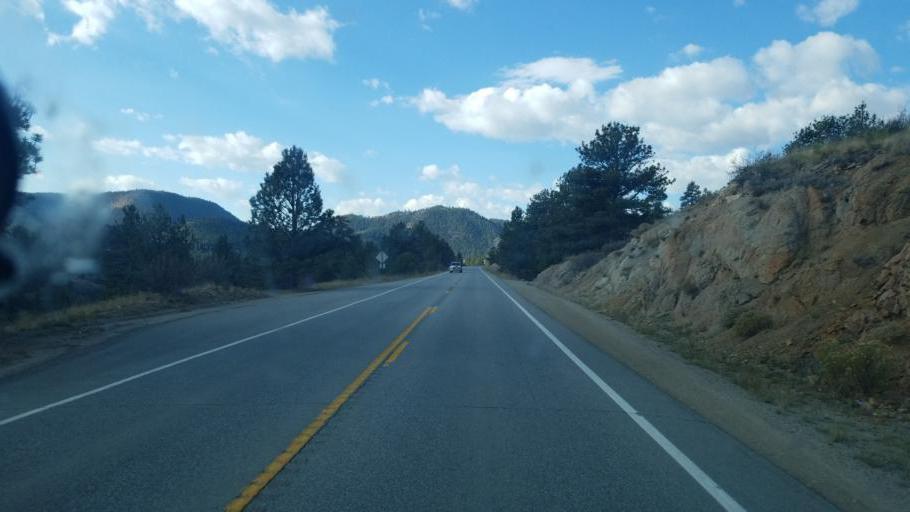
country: US
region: Colorado
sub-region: Chaffee County
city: Buena Vista
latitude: 38.8490
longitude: -105.9859
